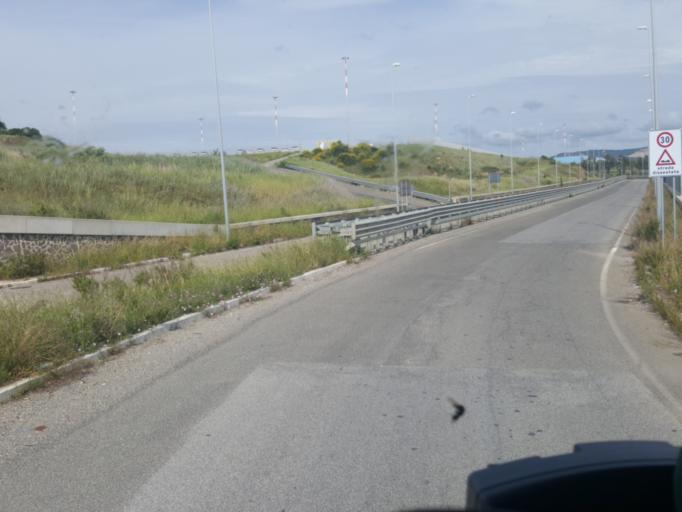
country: IT
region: Latium
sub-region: Citta metropolitana di Roma Capitale
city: Aurelia
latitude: 42.1246
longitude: 11.7786
